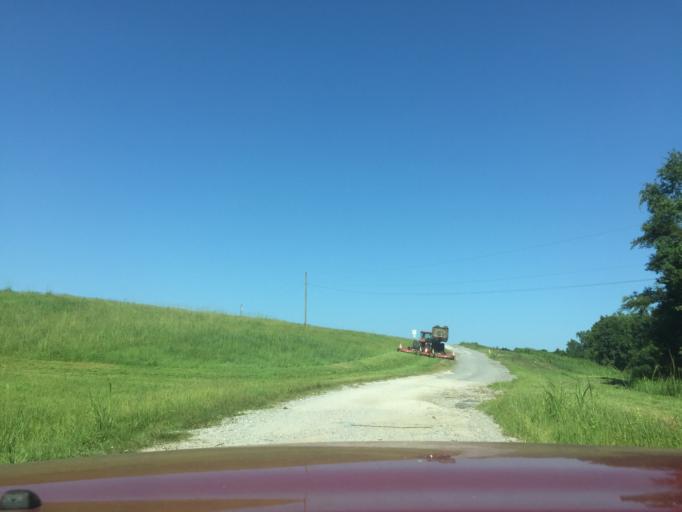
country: US
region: Georgia
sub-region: Chatham County
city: Garden City
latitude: 32.0846
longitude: -81.1704
